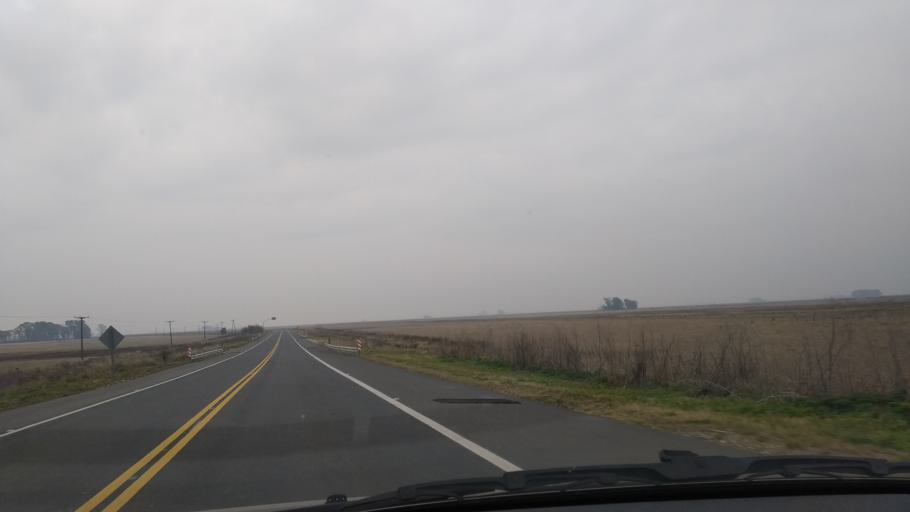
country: AR
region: Buenos Aires
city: Olavarria
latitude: -37.0114
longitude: -60.3960
